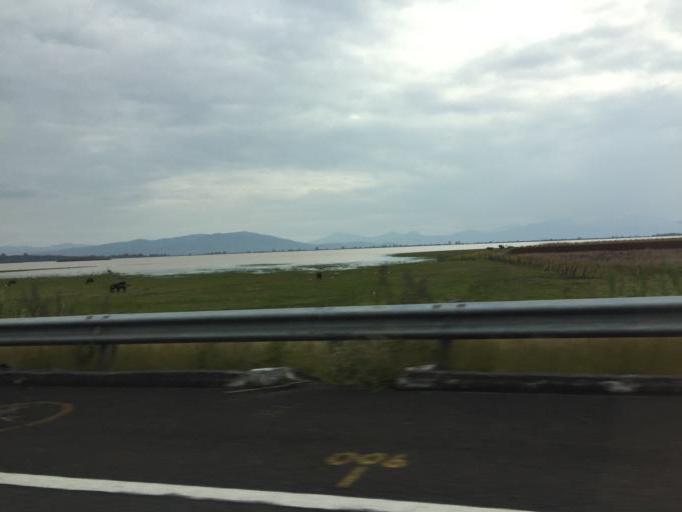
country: MX
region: Michoacan
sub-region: Puruandiro
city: San Lorenzo
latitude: 19.9486
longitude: -101.6432
